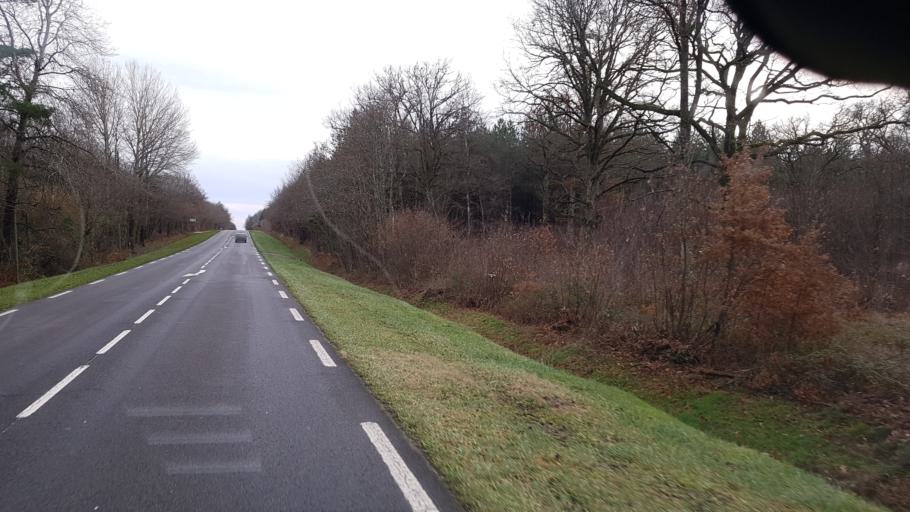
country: FR
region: Centre
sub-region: Departement du Loir-et-Cher
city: Lamotte-Beuvron
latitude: 47.6252
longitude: 2.0093
